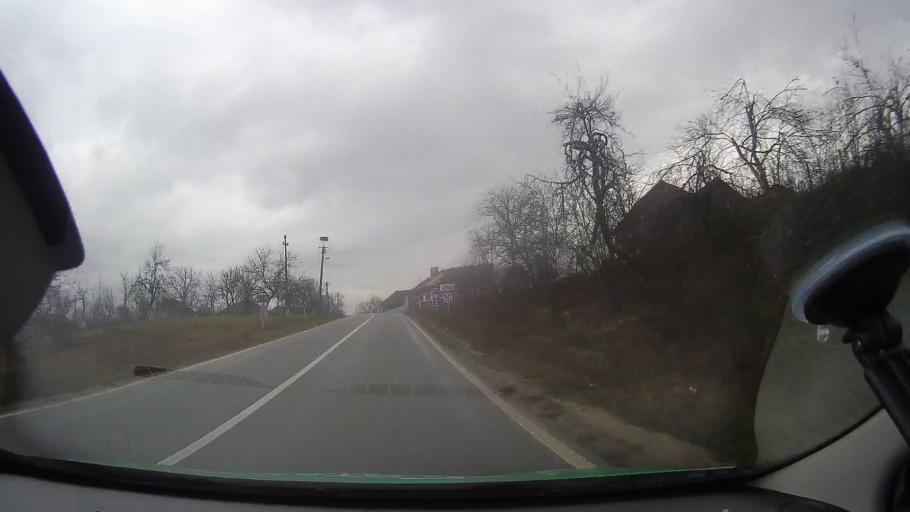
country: RO
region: Arad
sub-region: Comuna Almas
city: Almas
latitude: 46.2904
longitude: 22.2215
